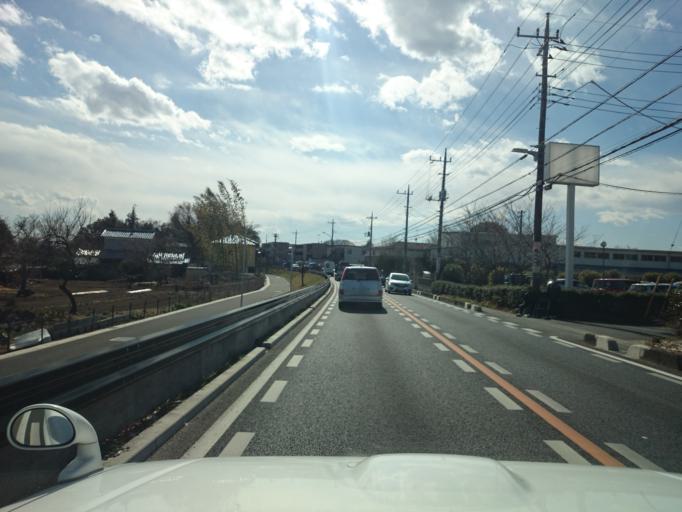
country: JP
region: Saitama
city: Kukichuo
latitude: 36.0551
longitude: 139.7018
